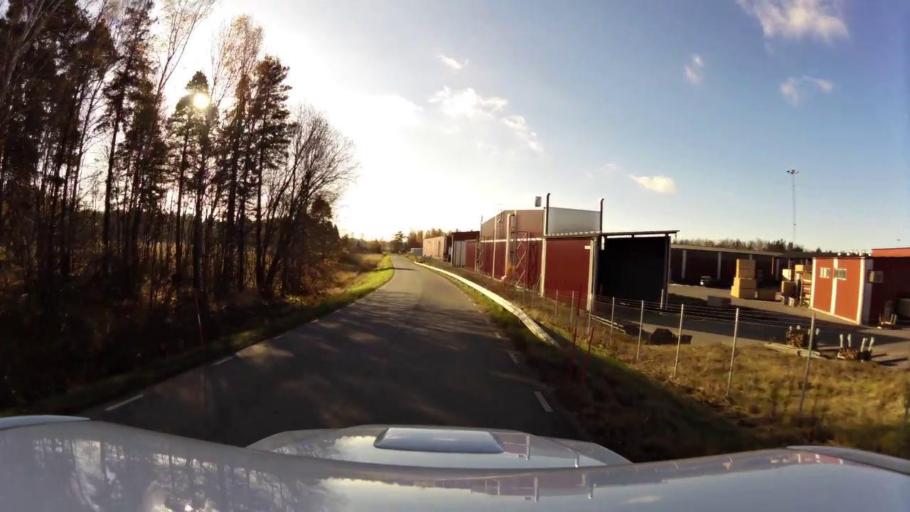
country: SE
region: OEstergoetland
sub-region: Linkopings Kommun
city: Linghem
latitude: 58.4414
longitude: 15.7789
